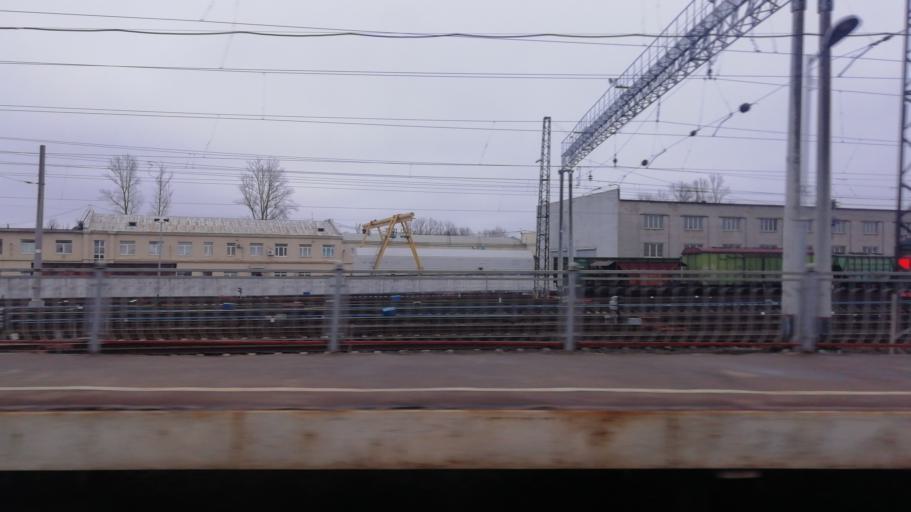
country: RU
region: St.-Petersburg
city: Kupchino
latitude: 59.8902
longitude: 30.3456
